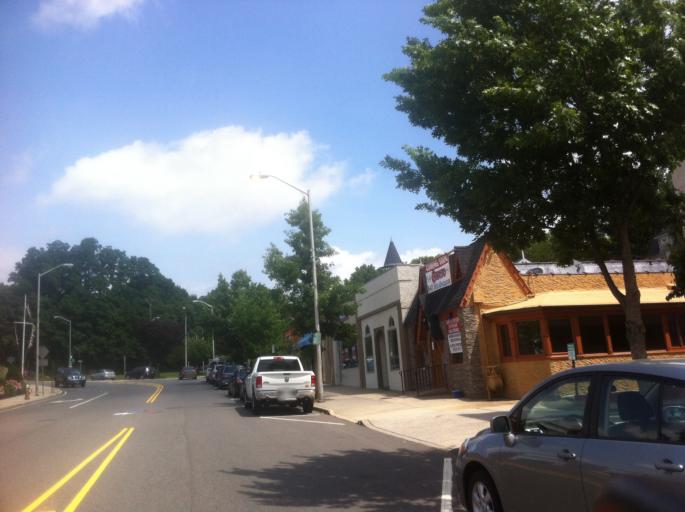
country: US
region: New York
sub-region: Nassau County
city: Glen Cove
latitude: 40.8672
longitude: -73.6307
